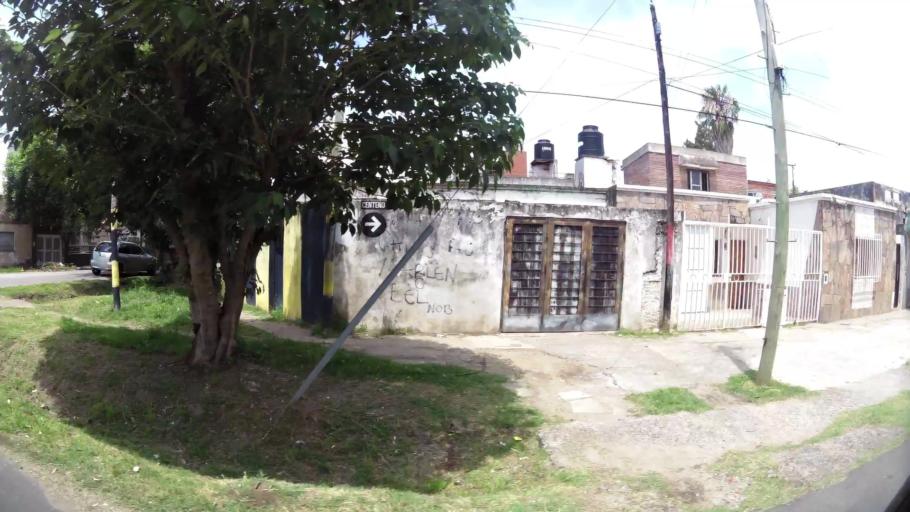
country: AR
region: Santa Fe
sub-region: Departamento de Rosario
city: Rosario
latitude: -32.9881
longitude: -60.6299
